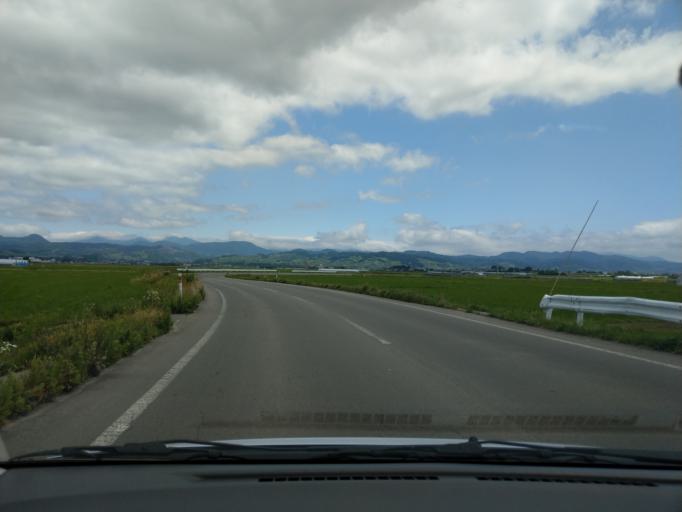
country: JP
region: Aomori
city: Kuroishi
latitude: 40.6303
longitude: 140.5624
